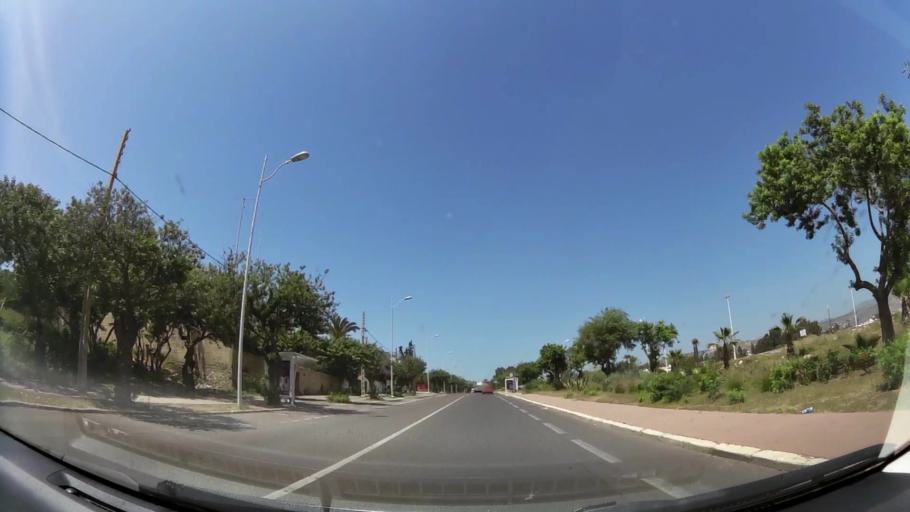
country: MA
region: Souss-Massa-Draa
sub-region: Agadir-Ida-ou-Tnan
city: Agadir
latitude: 30.4310
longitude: -9.5933
